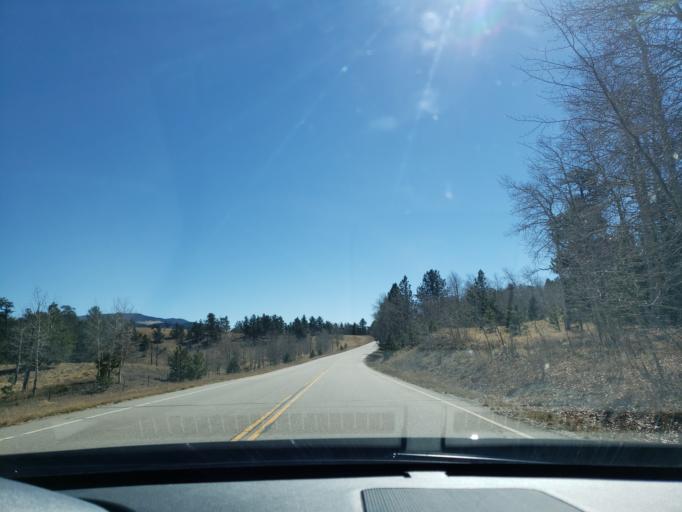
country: US
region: Colorado
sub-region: Chaffee County
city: Buena Vista
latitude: 38.8862
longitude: -105.6822
